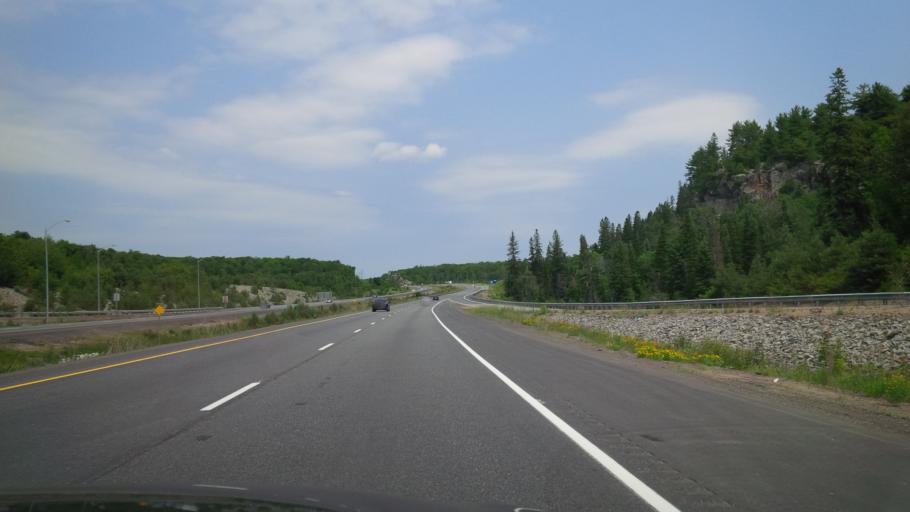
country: CA
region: Ontario
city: Huntsville
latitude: 45.4132
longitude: -79.2392
